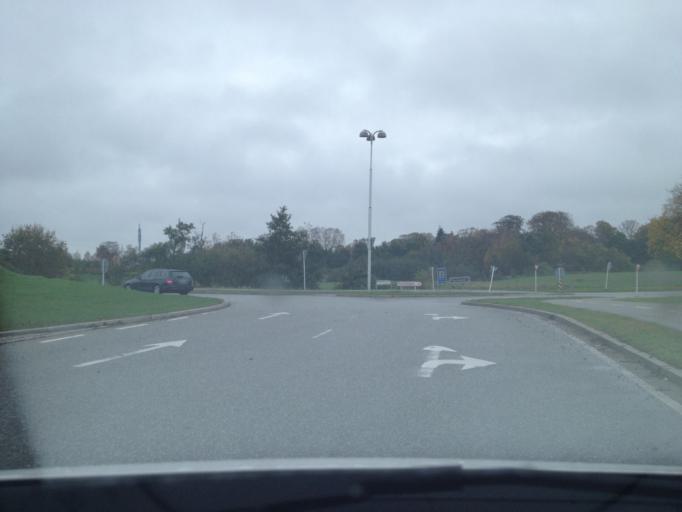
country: DK
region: Capital Region
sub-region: Fredensborg Kommune
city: Fredensborg
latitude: 55.9648
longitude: 12.4068
